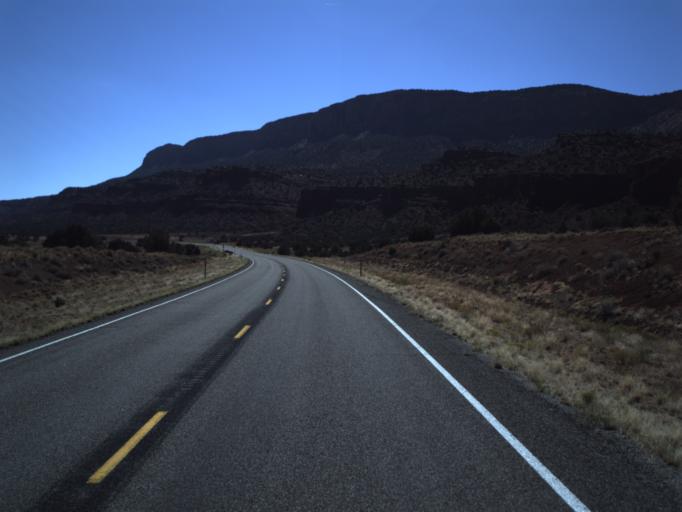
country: US
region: Utah
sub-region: San Juan County
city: Blanding
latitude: 37.6850
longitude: -110.2217
